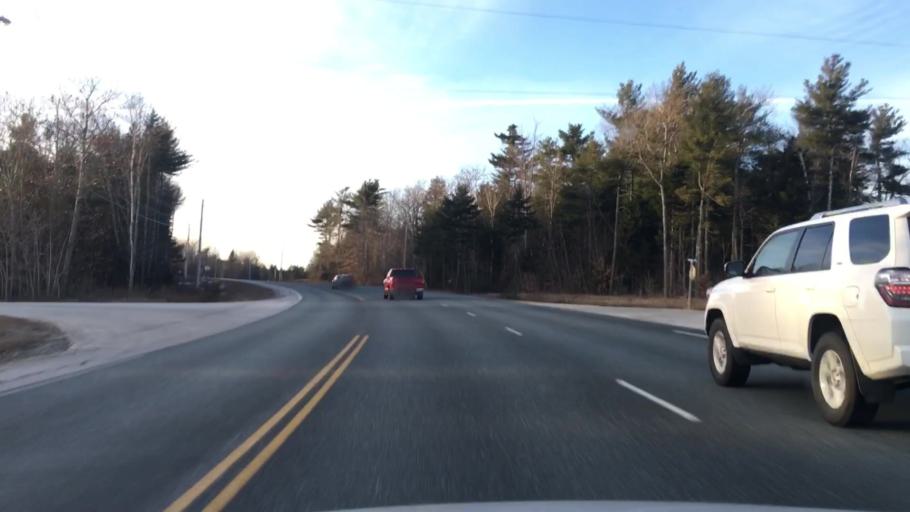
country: US
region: Maine
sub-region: Hancock County
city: Dedham
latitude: 44.6444
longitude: -68.5559
